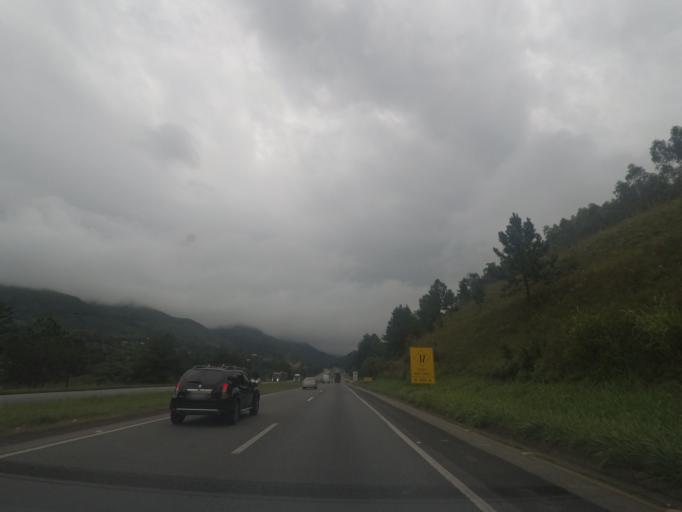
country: BR
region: Parana
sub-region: Campina Grande Do Sul
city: Campina Grande do Sul
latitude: -25.1289
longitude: -48.8575
